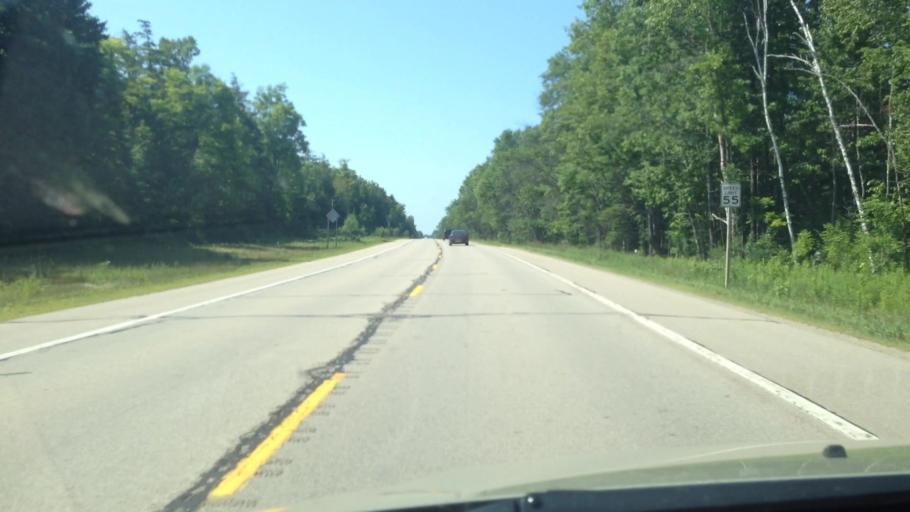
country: US
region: Michigan
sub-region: Menominee County
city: Menominee
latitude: 45.4051
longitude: -87.3614
